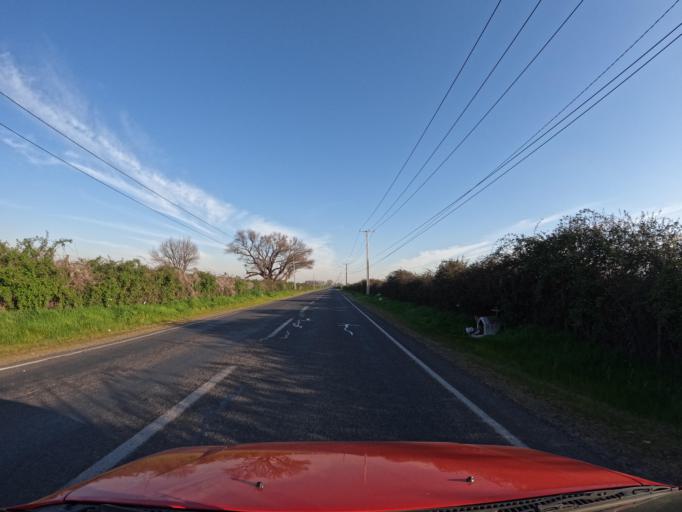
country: CL
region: Maule
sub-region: Provincia de Curico
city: Rauco
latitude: -34.9208
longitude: -71.2771
